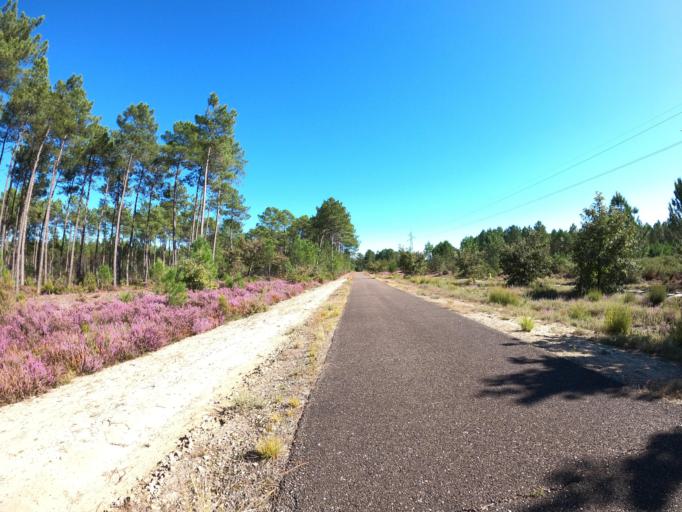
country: FR
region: Aquitaine
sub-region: Departement des Landes
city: Ychoux
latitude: 44.3370
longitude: -0.9527
